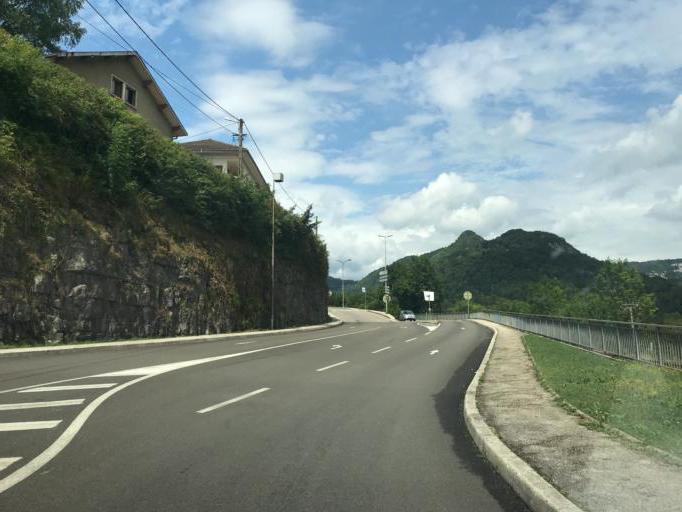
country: FR
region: Franche-Comte
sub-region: Departement du Jura
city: Saint-Claude
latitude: 46.3966
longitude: 5.8633
